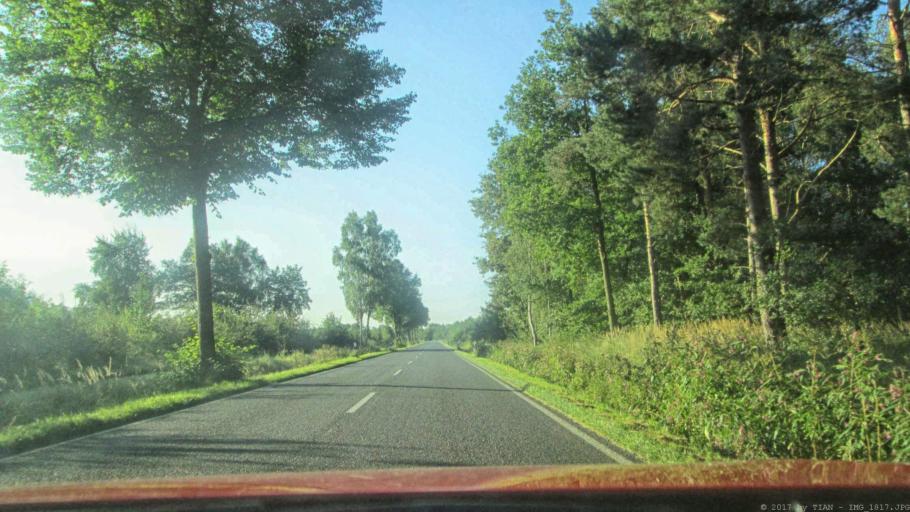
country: DE
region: Lower Saxony
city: Wolfsburg
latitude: 52.4616
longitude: 10.8223
